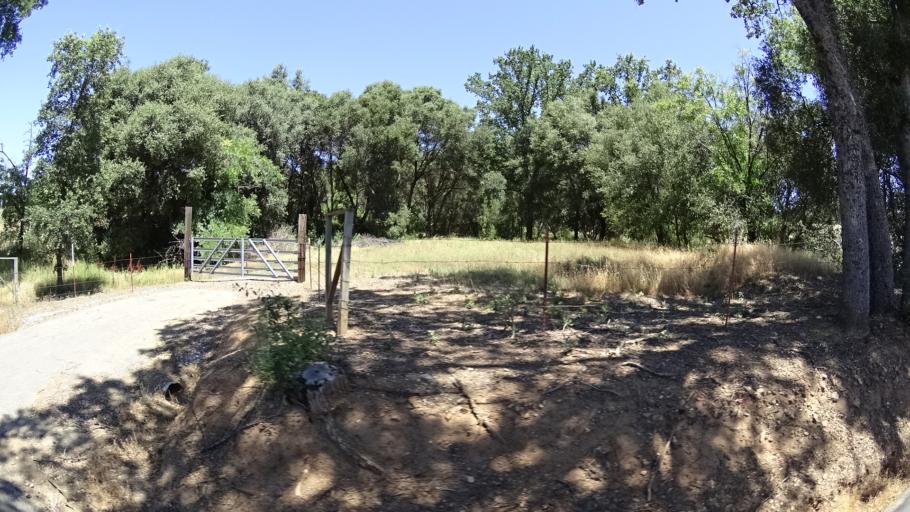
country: US
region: California
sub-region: Calaveras County
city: Mountain Ranch
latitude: 38.2320
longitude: -120.5496
